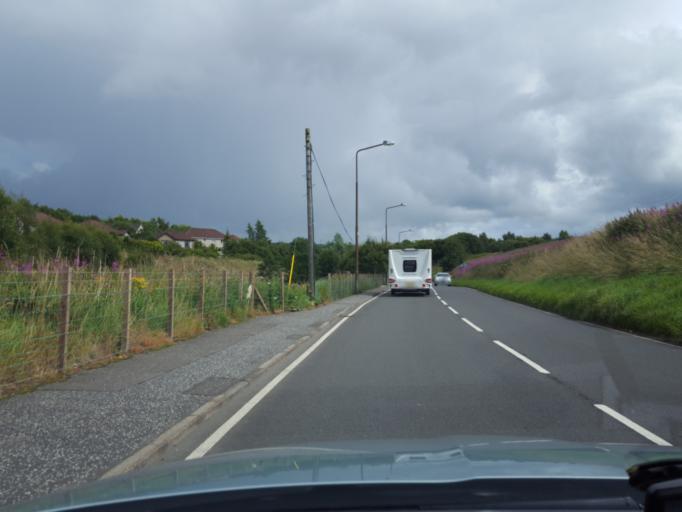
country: GB
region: Scotland
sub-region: West Lothian
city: Bathgate
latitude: 55.9078
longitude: -3.6565
